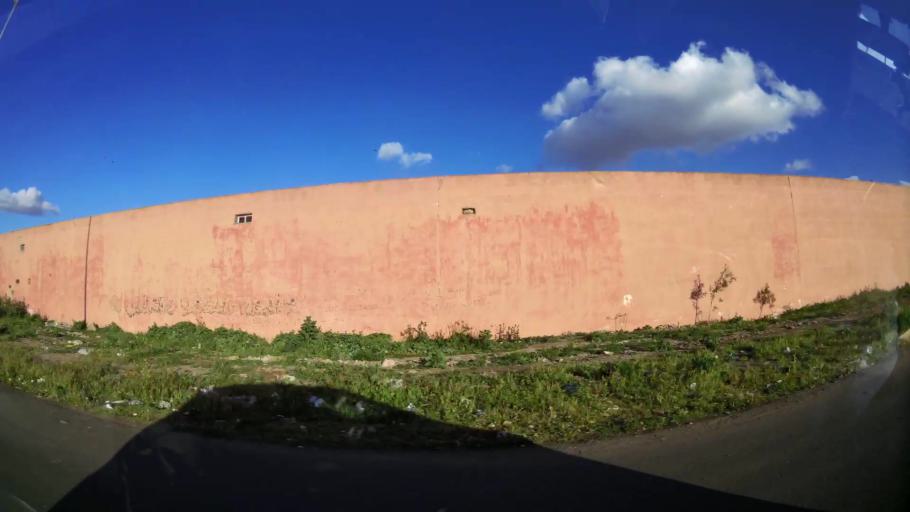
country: MA
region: Marrakech-Tensift-Al Haouz
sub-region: Kelaa-Des-Sraghna
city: Sidi Abdallah
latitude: 32.2390
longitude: -7.9650
